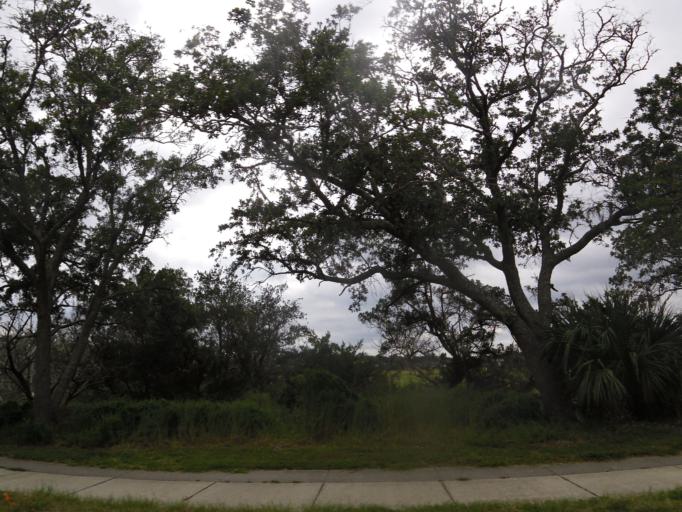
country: US
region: Georgia
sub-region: Glynn County
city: Saint Simons Island
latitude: 31.1474
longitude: -81.3742
